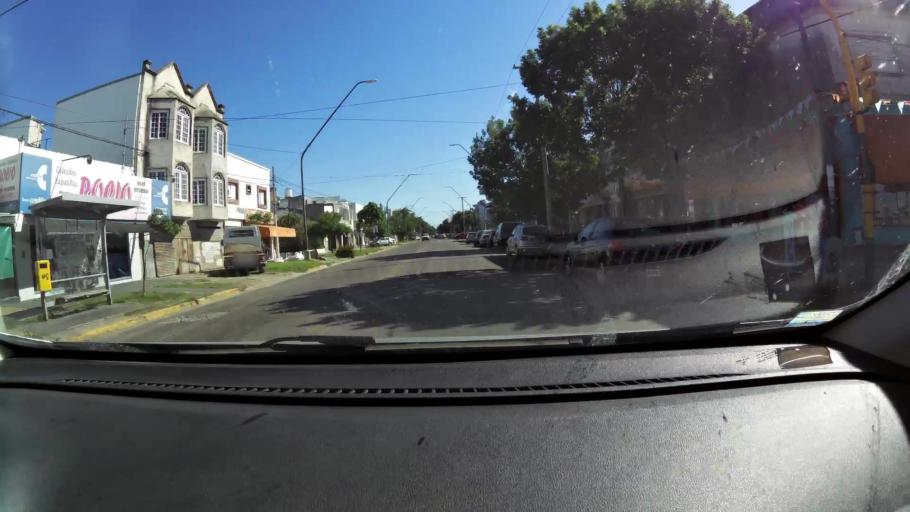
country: AR
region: Santa Fe
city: Santa Fe de la Vera Cruz
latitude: -31.6218
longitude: -60.6869
